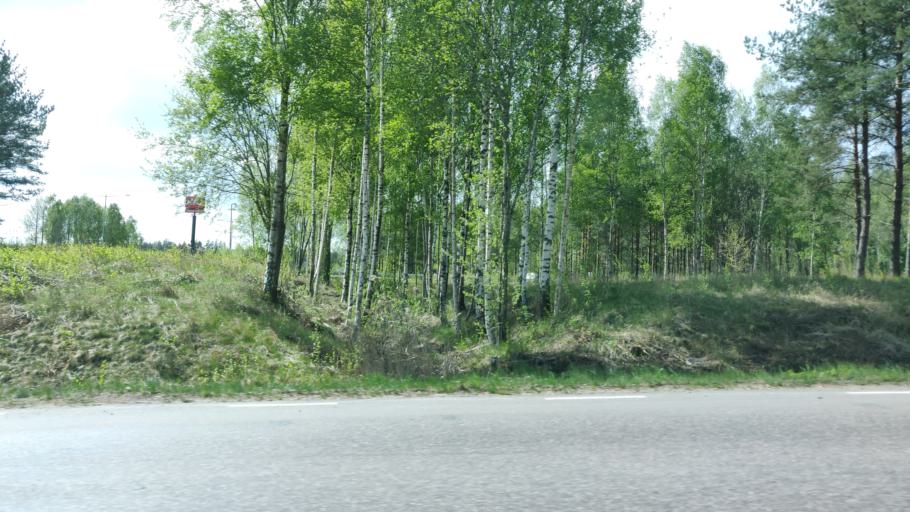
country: SE
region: Vaermland
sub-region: Karlstads Kommun
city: Skattkarr
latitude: 59.3989
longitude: 13.5824
